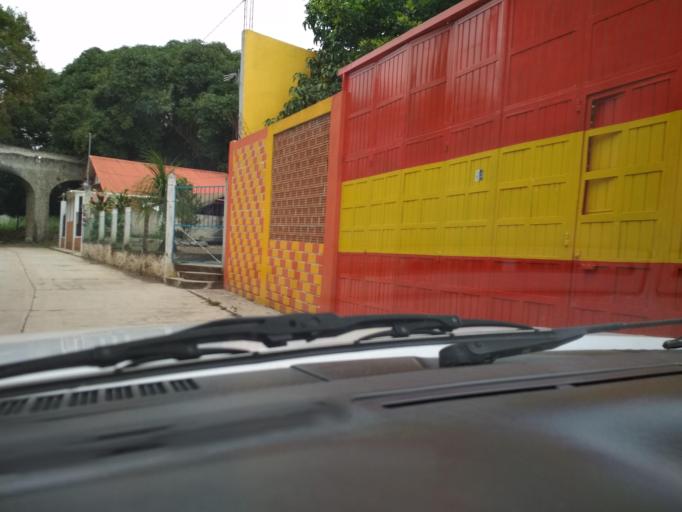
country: MX
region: Veracruz
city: Alto Lucero
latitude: 19.5919
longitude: -96.7823
